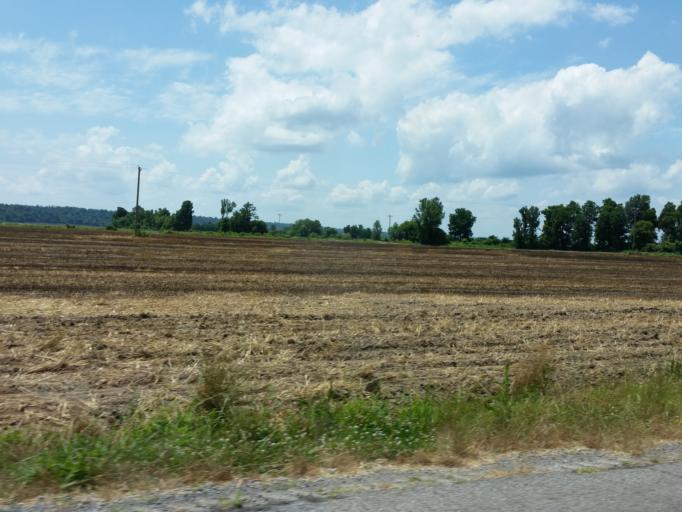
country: US
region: Kentucky
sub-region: Fulton County
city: Hickman
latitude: 36.5481
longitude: -89.2488
